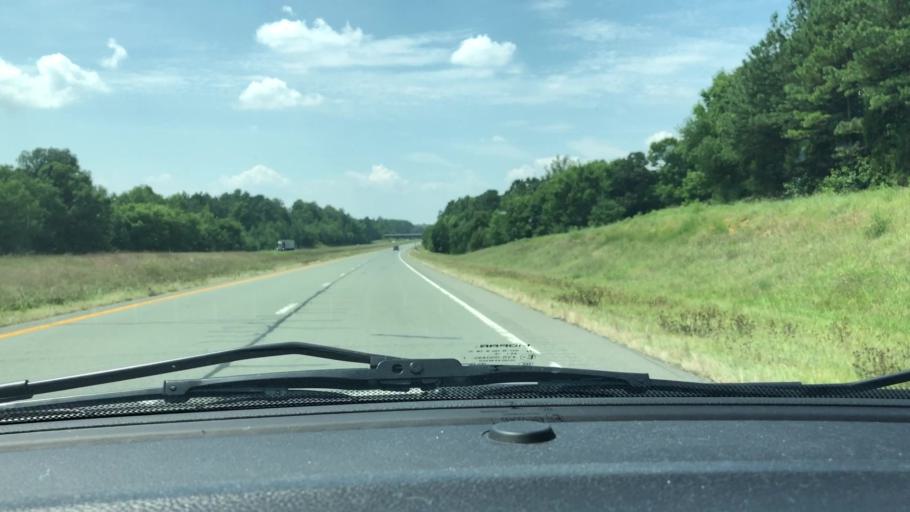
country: US
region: North Carolina
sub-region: Randolph County
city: Liberty
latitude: 35.7922
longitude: -79.5285
